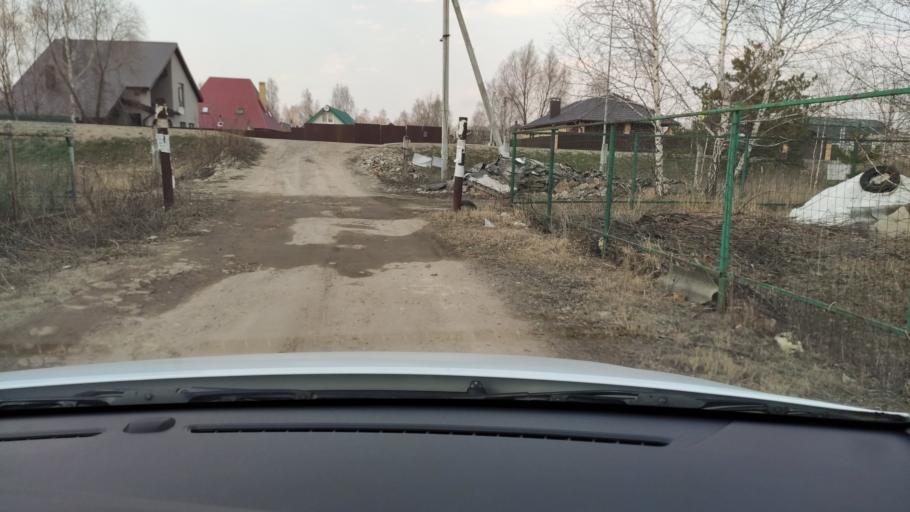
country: RU
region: Tatarstan
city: Stolbishchi
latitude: 55.6940
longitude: 49.2020
